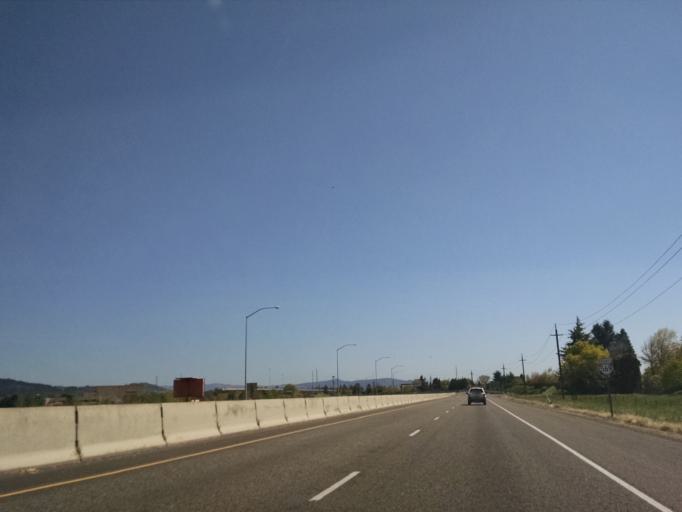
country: US
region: Oregon
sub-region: Lane County
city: Eugene
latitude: 44.0863
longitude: -123.0609
